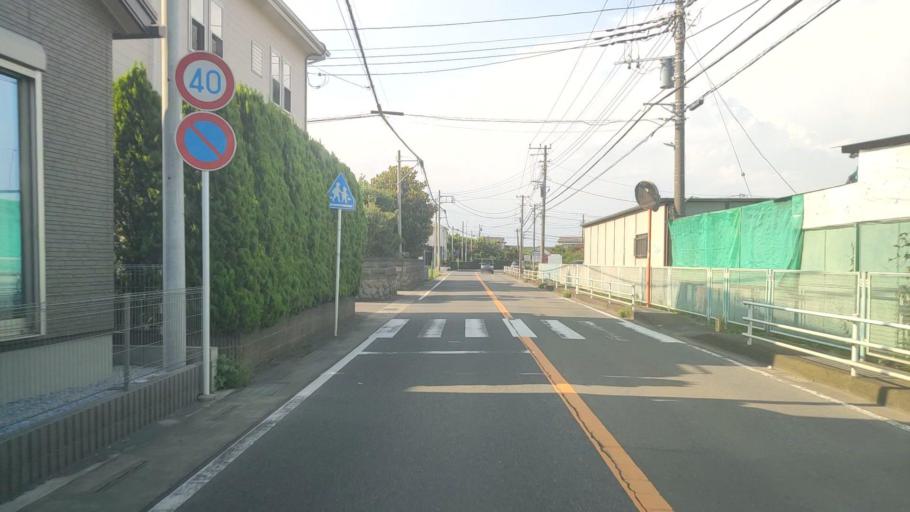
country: JP
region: Kanagawa
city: Isehara
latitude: 35.3743
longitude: 139.3328
